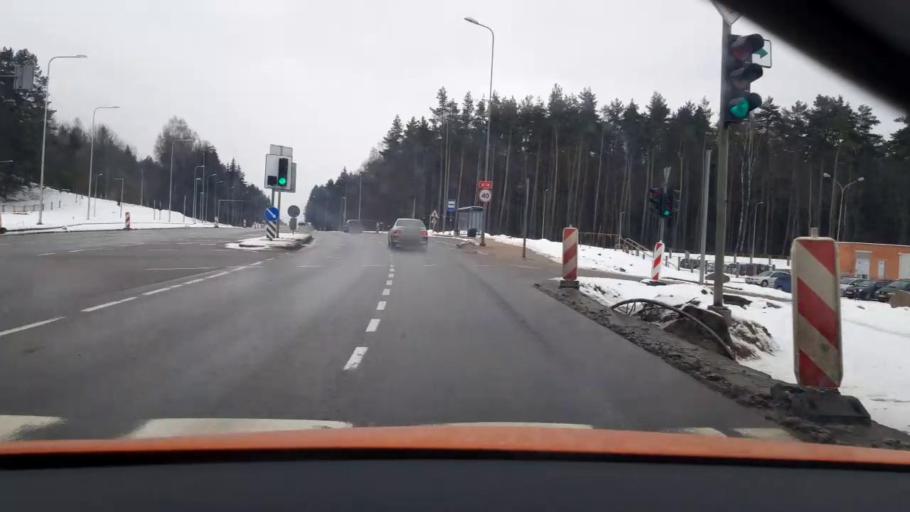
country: LT
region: Vilnius County
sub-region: Vilnius
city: Fabijoniskes
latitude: 54.7569
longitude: 25.2721
